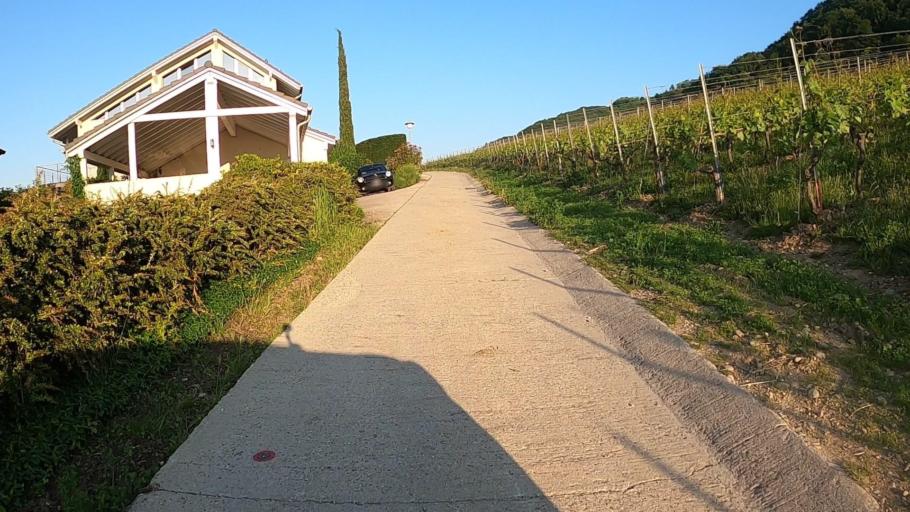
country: CH
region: Vaud
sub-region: Nyon District
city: Rolle
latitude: 46.4759
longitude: 6.3394
